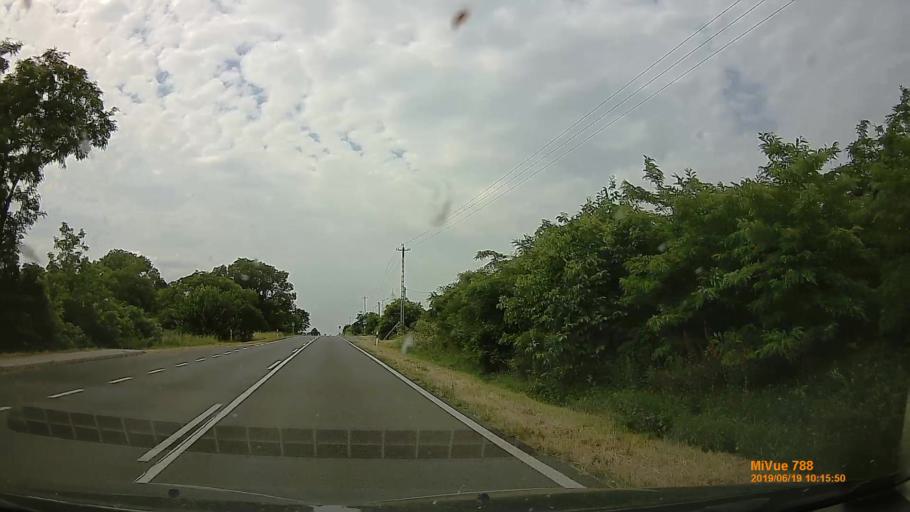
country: HU
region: Fejer
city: Baracs
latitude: 46.8513
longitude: 18.9120
